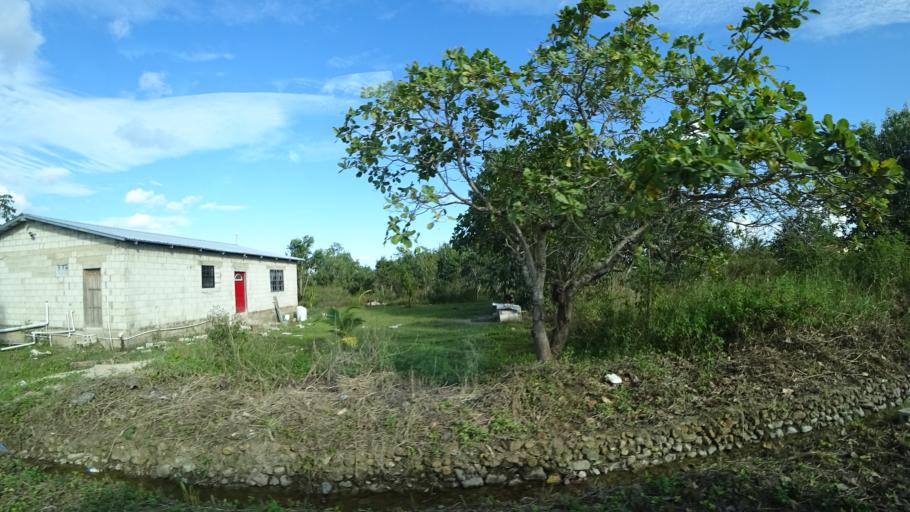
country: BZ
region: Belize
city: Belize City
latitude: 17.5555
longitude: -88.4017
